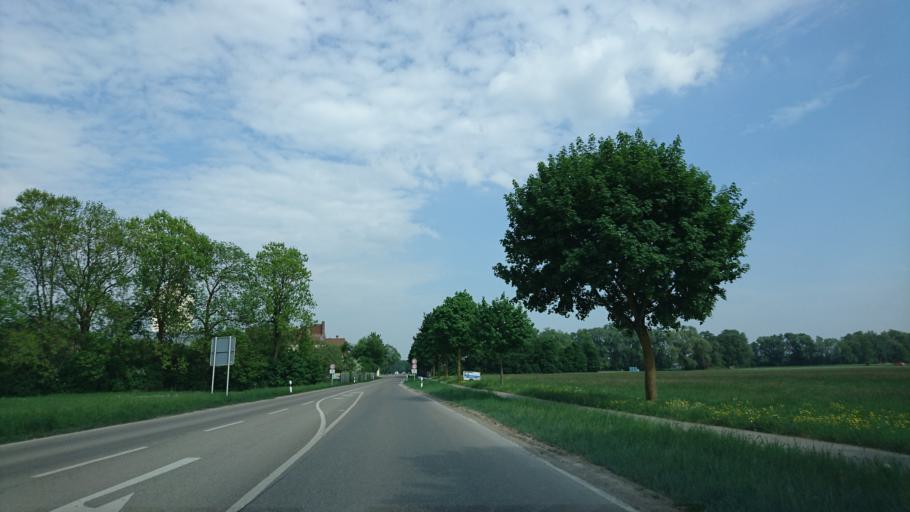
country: DE
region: Bavaria
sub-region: Swabia
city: Gersthofen
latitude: 48.4244
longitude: 10.8978
